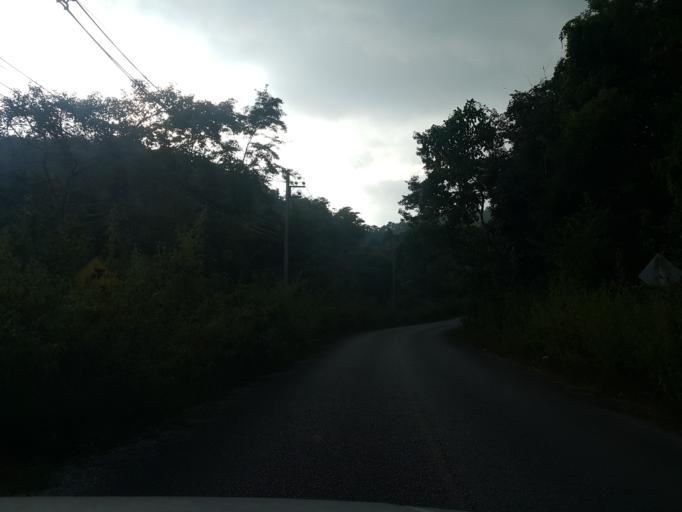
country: TH
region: Chiang Mai
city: Mae Chaem
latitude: 18.7403
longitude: 98.2231
